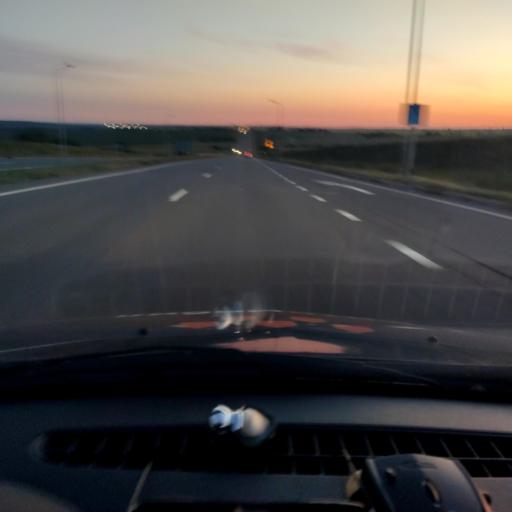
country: RU
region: Belgorod
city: Staryy Oskol
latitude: 51.3257
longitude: 37.7353
